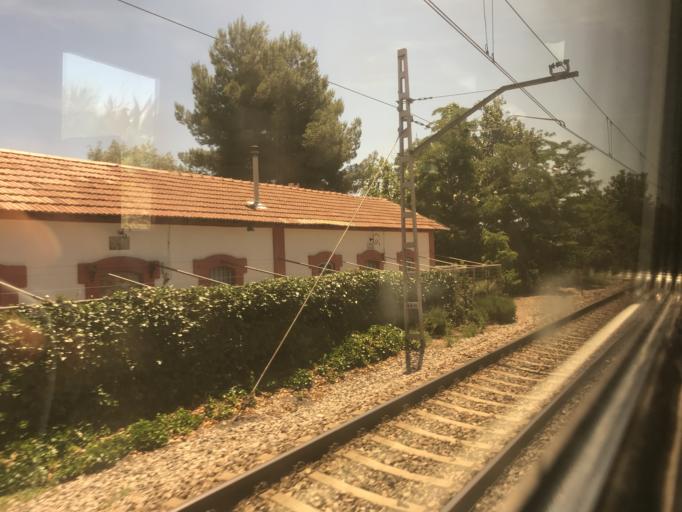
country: ES
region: Madrid
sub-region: Provincia de Madrid
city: Aranjuez
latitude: 40.0456
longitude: -3.6218
